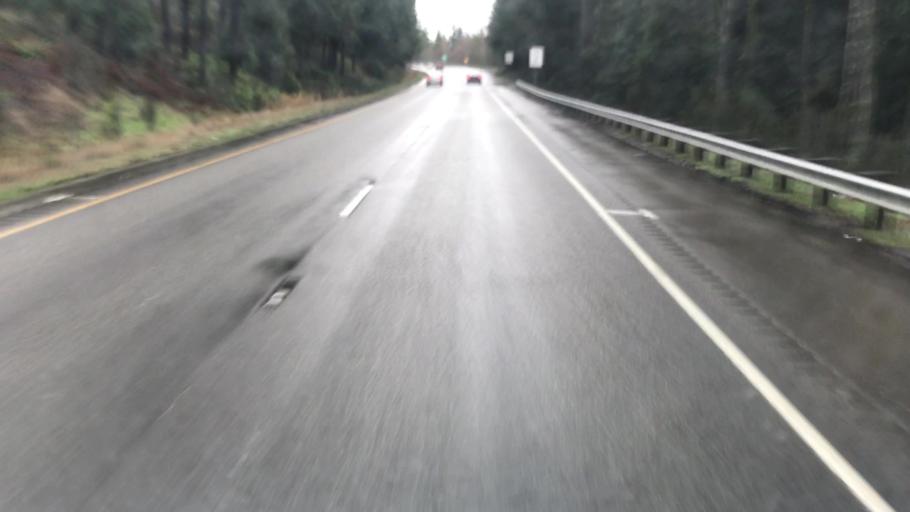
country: US
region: Washington
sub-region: Kitsap County
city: Burley
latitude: 47.4264
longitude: -122.6239
